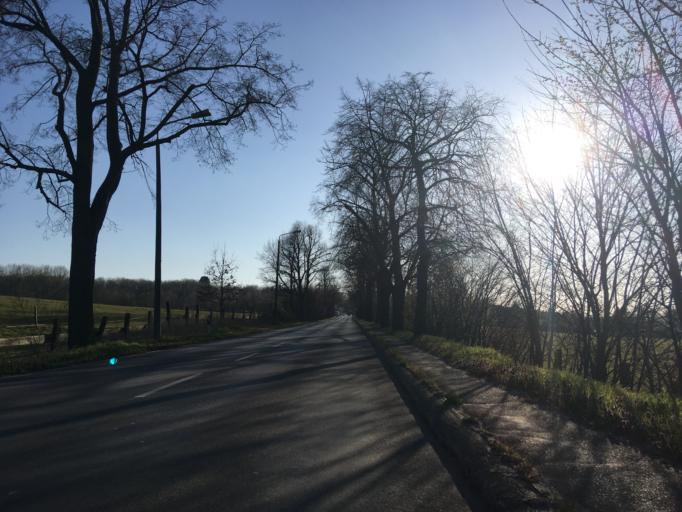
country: DE
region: Berlin
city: Buch
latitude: 52.6432
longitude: 13.5202
